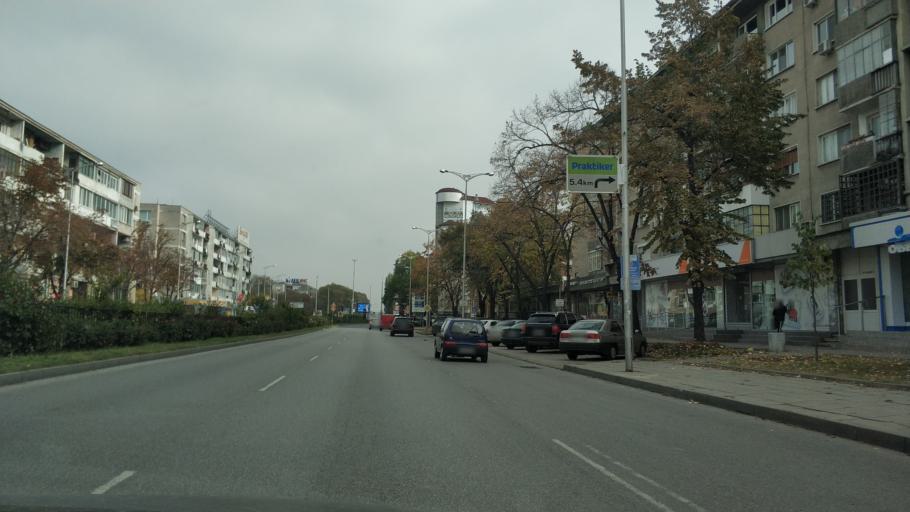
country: BG
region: Plovdiv
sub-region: Obshtina Plovdiv
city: Plovdiv
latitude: 42.1590
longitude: 24.7459
